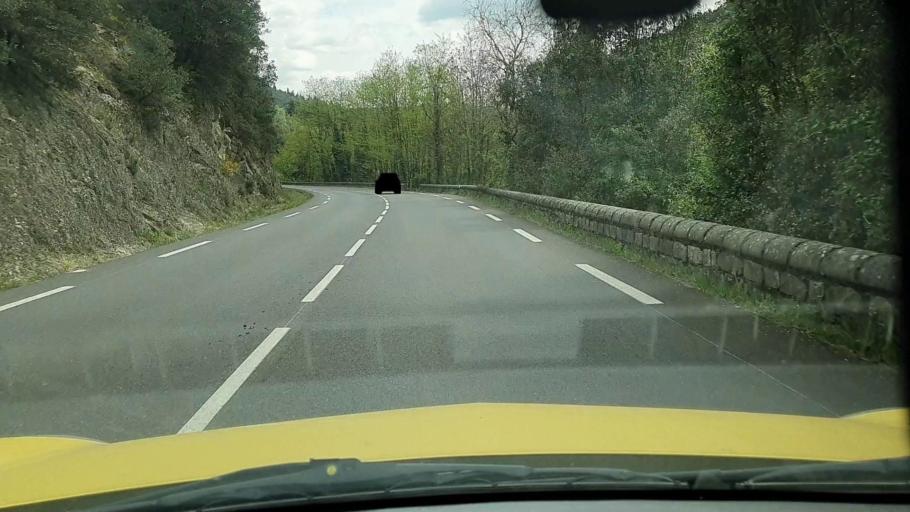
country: FR
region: Languedoc-Roussillon
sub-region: Departement du Gard
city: Valleraugue
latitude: 44.0641
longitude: 3.6814
